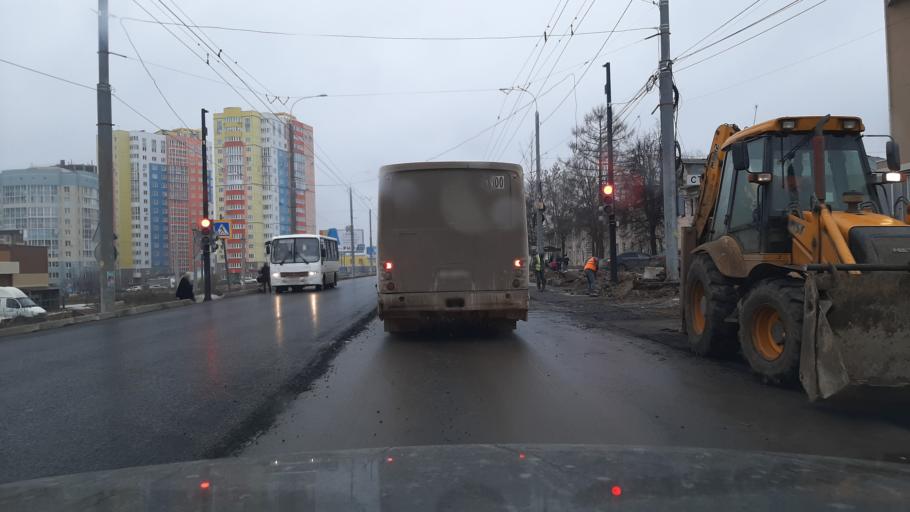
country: RU
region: Ivanovo
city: Kokhma
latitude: 56.9411
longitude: 41.0619
